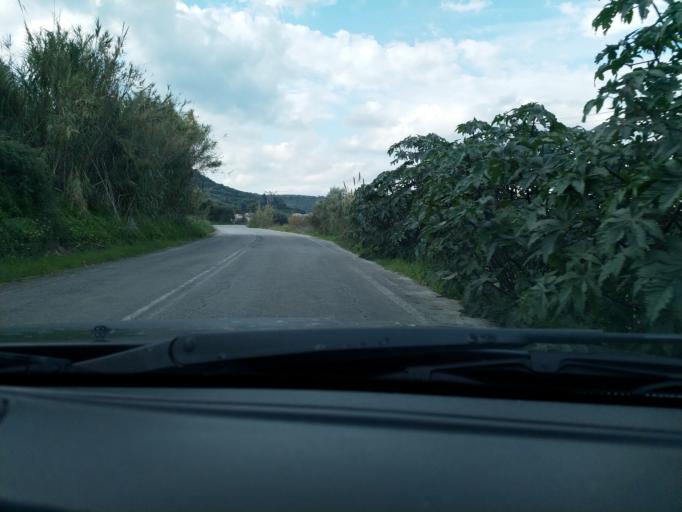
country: GR
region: Crete
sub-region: Nomos Chanias
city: Agia Marina
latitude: 35.4975
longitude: 23.9038
